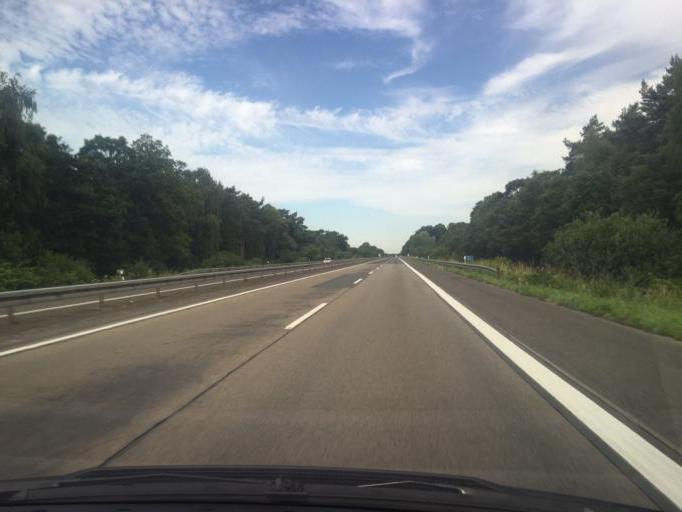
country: DE
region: North Rhine-Westphalia
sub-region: Regierungsbezirk Dusseldorf
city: Issum
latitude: 51.5717
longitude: 6.4429
